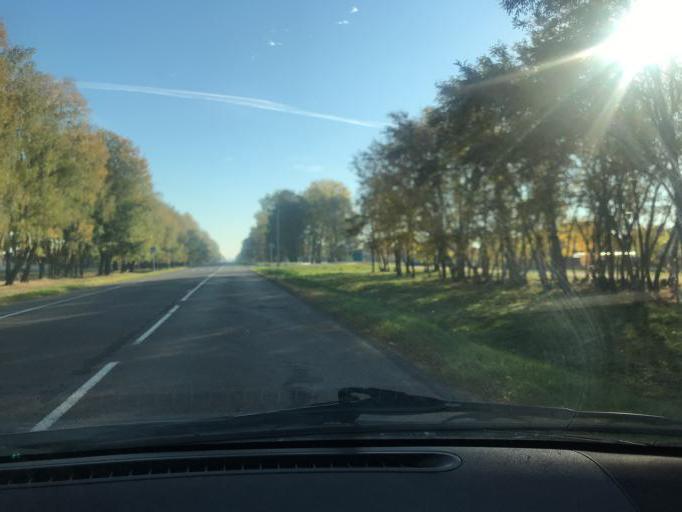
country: BY
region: Brest
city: Ivanava
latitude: 52.1445
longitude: 25.4924
